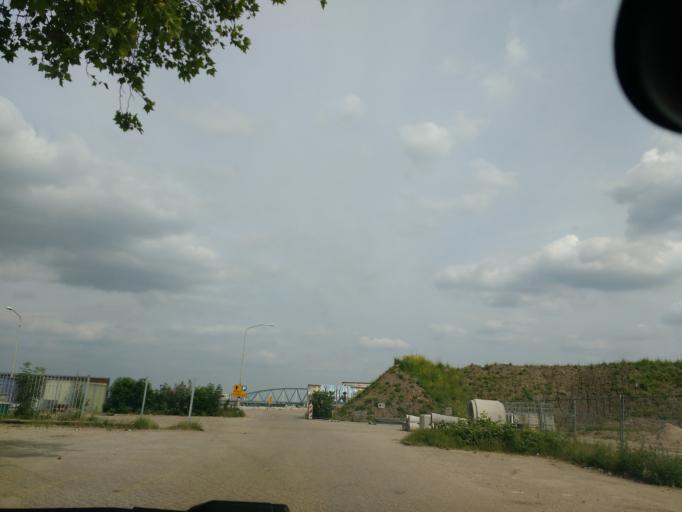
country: NL
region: Gelderland
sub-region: Gemeente Nijmegen
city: Nijmegen
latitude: 51.8553
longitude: 5.8422
